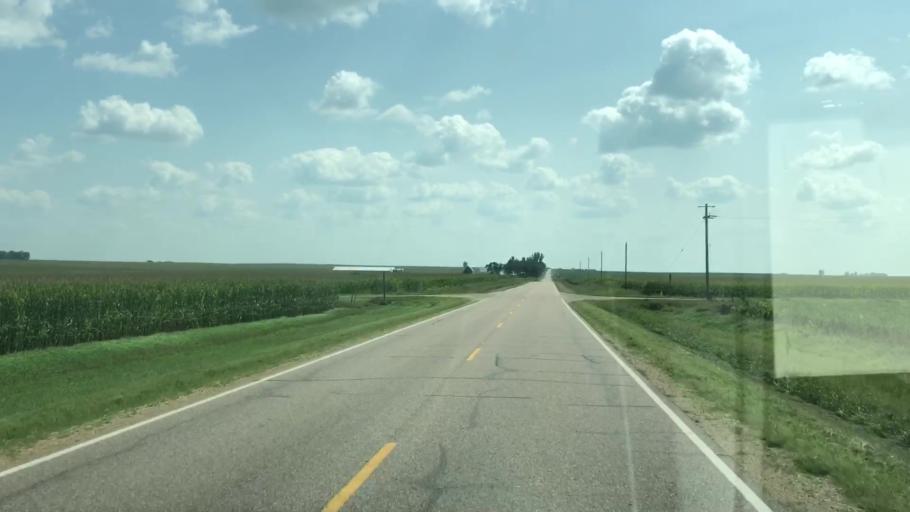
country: US
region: Iowa
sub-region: O'Brien County
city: Sheldon
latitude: 43.1577
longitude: -95.8019
